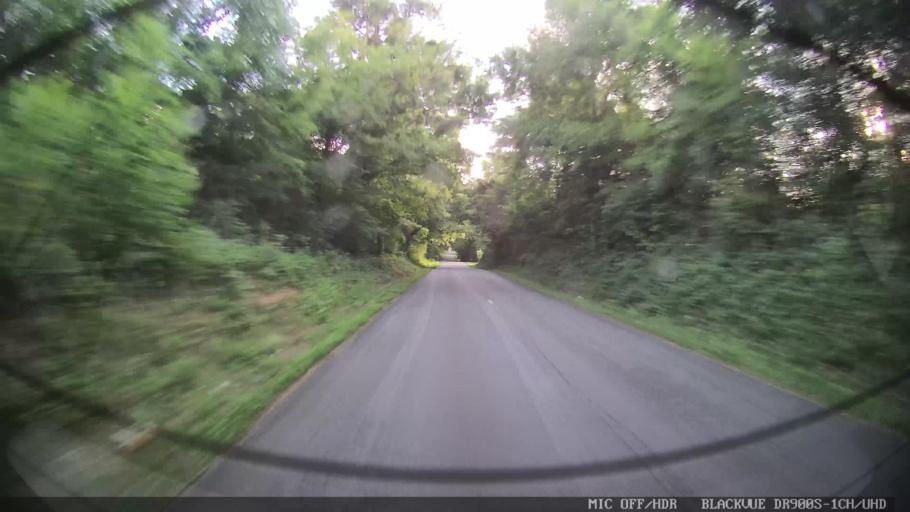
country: US
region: Georgia
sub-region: Bartow County
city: Rydal
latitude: 34.2960
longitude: -84.7361
